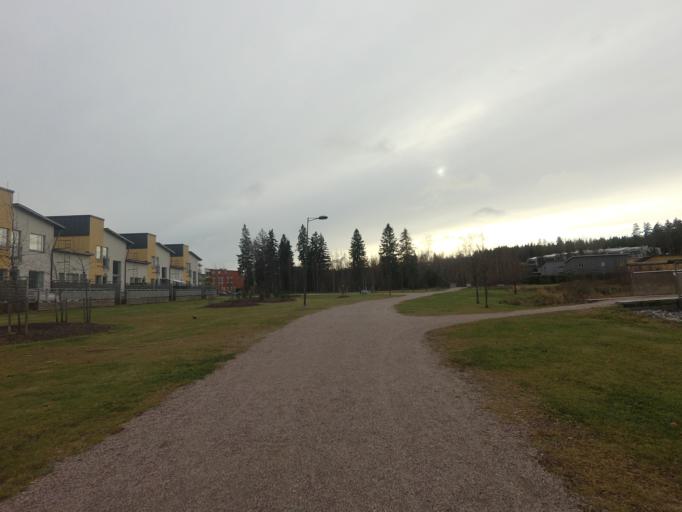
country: FI
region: Uusimaa
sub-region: Helsinki
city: Kauniainen
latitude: 60.1876
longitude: 24.7375
